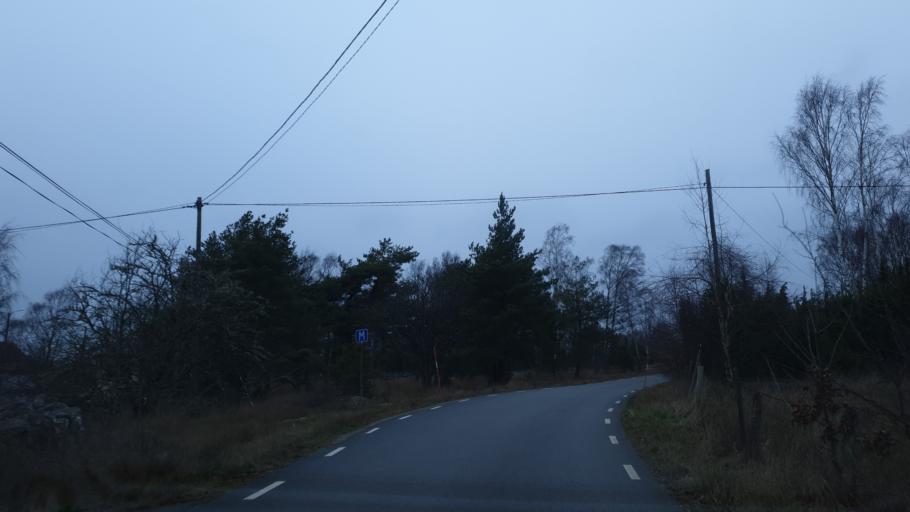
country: SE
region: Blekinge
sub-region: Karlskrona Kommun
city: Karlskrona
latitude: 56.1089
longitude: 15.6112
